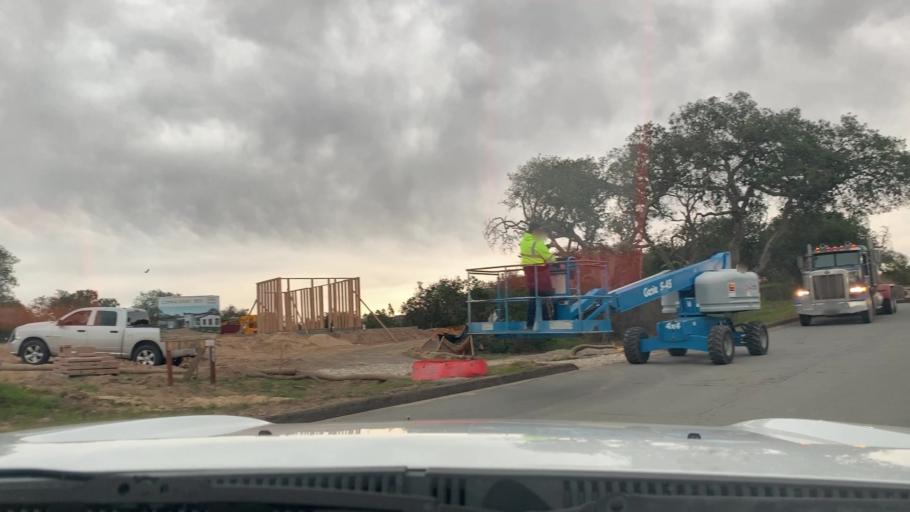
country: US
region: California
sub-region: San Luis Obispo County
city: Callender
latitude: 35.0667
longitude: -120.5601
